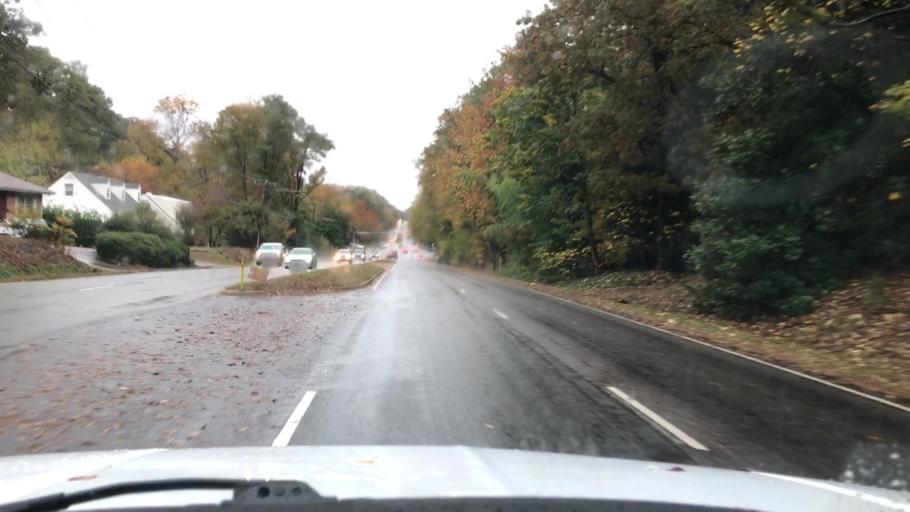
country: US
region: Virginia
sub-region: Henrico County
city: Tuckahoe
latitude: 37.5939
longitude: -77.5528
